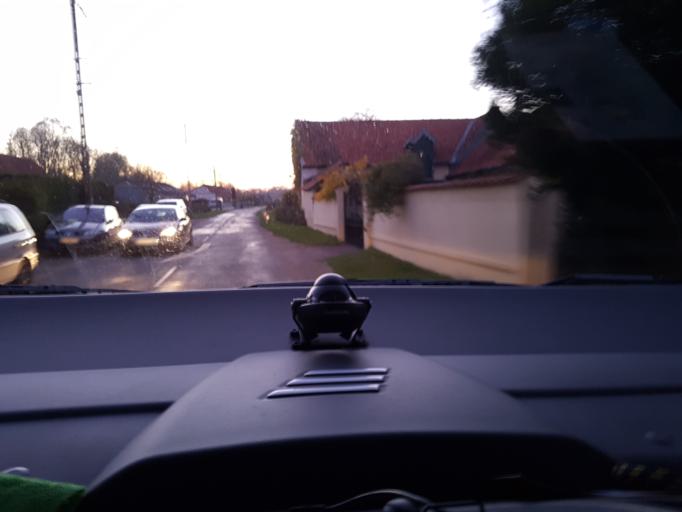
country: FR
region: Picardie
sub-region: Departement de la Somme
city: Rue
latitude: 50.2145
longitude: 1.7058
